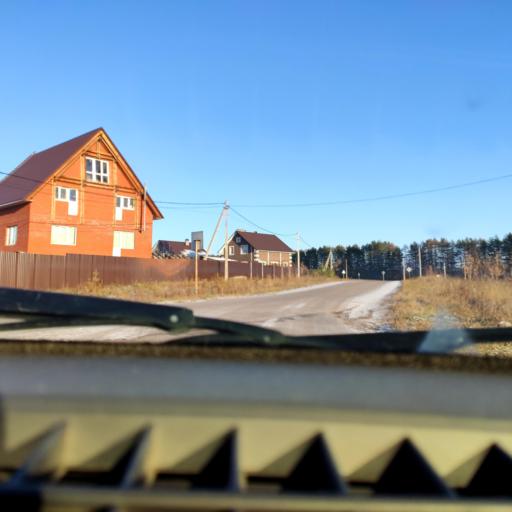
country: RU
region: Bashkortostan
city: Avdon
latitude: 54.6560
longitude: 55.7489
